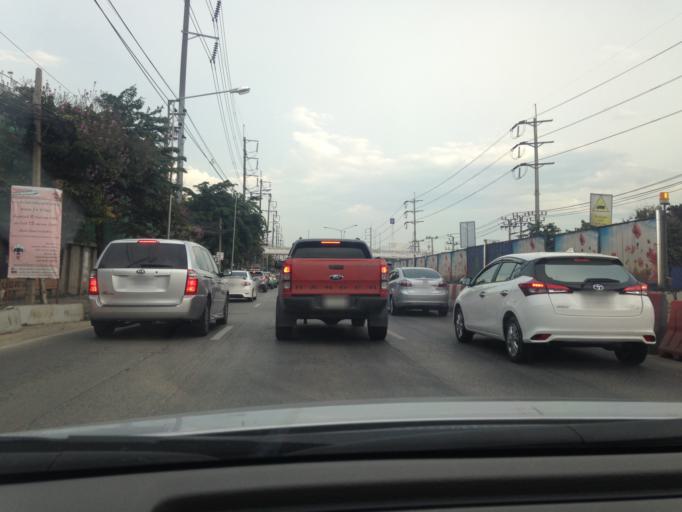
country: TH
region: Bangkok
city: Bang Khen
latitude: 13.8608
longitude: 100.6217
